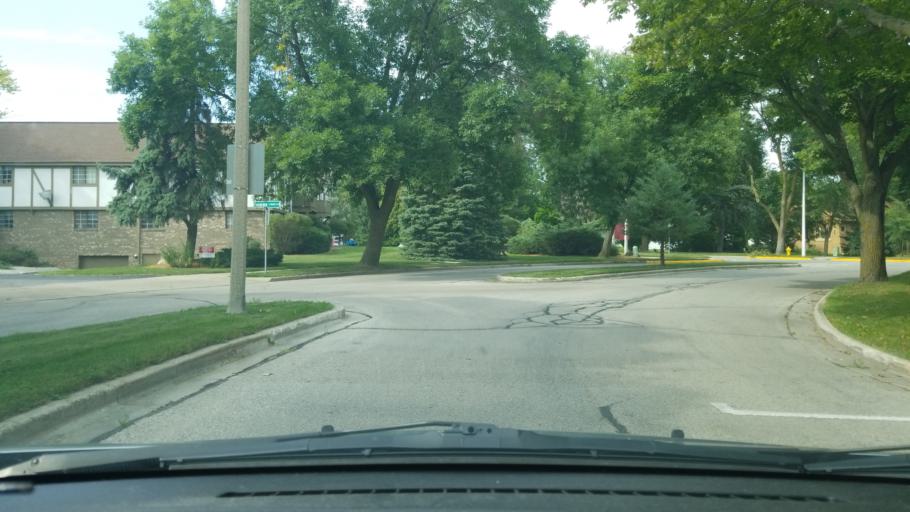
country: US
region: Wisconsin
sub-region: Ozaukee County
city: Cedarburg
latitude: 43.3072
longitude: -87.9946
